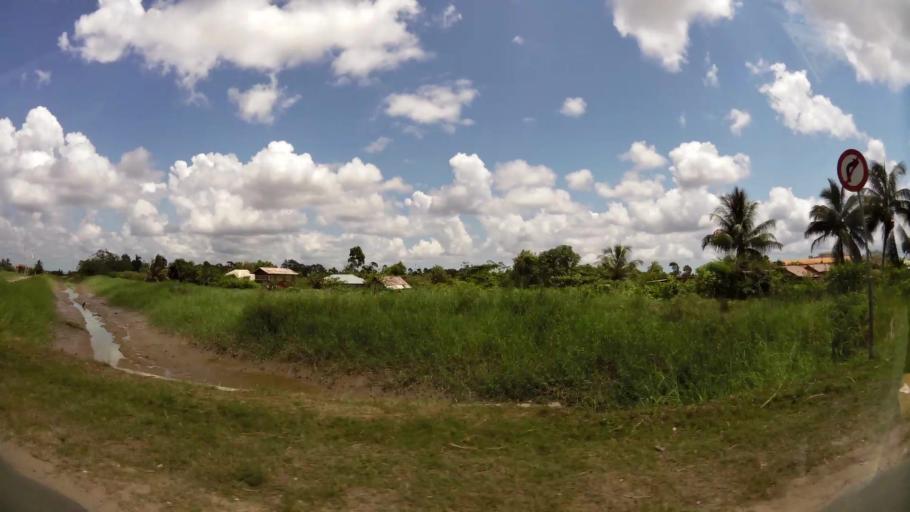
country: SR
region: Paramaribo
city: Paramaribo
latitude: 5.8078
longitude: -55.1547
